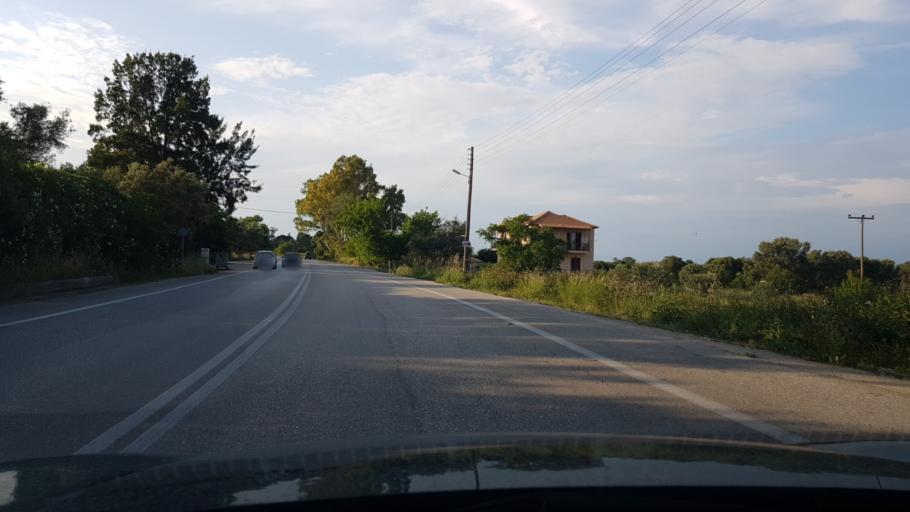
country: GR
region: Ionian Islands
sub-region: Lefkada
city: Lefkada
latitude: 38.8096
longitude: 20.7160
